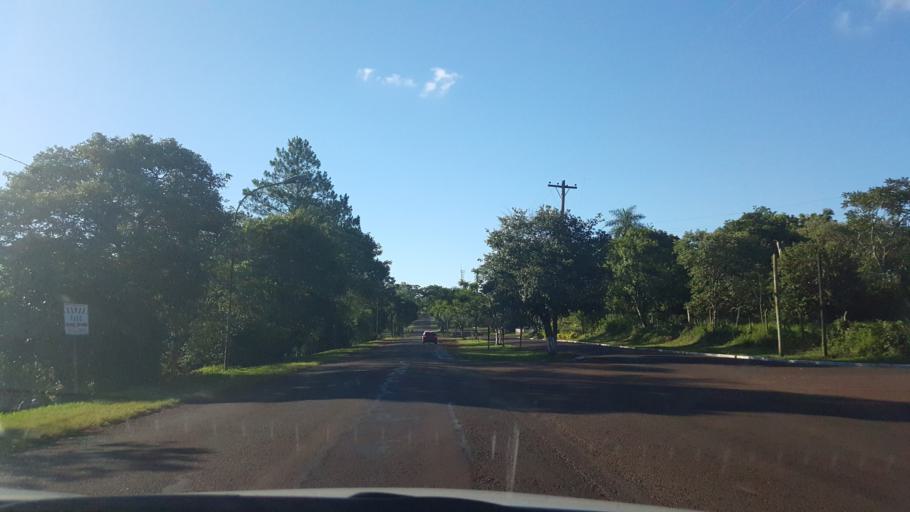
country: AR
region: Misiones
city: Gobernador Roca
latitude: -27.1327
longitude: -55.5072
